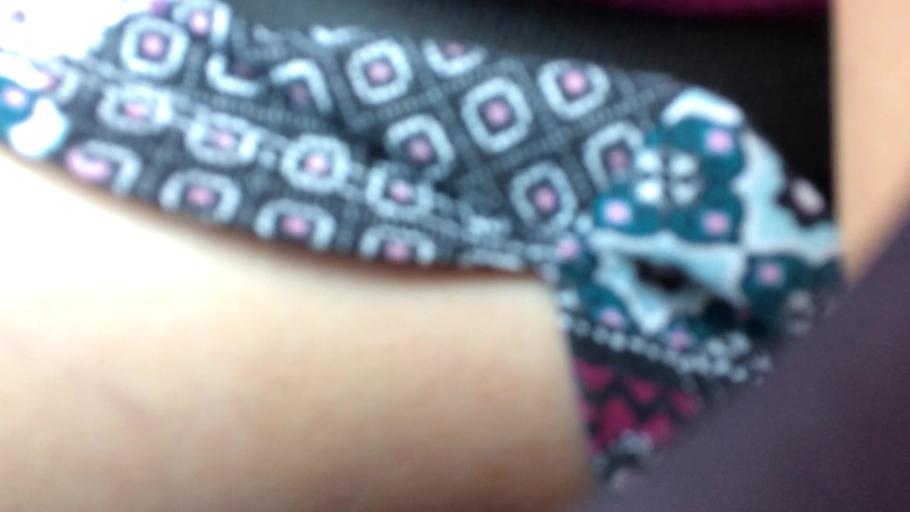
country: US
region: New Mexico
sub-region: Colfax County
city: Springer
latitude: 36.0665
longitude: -104.6910
